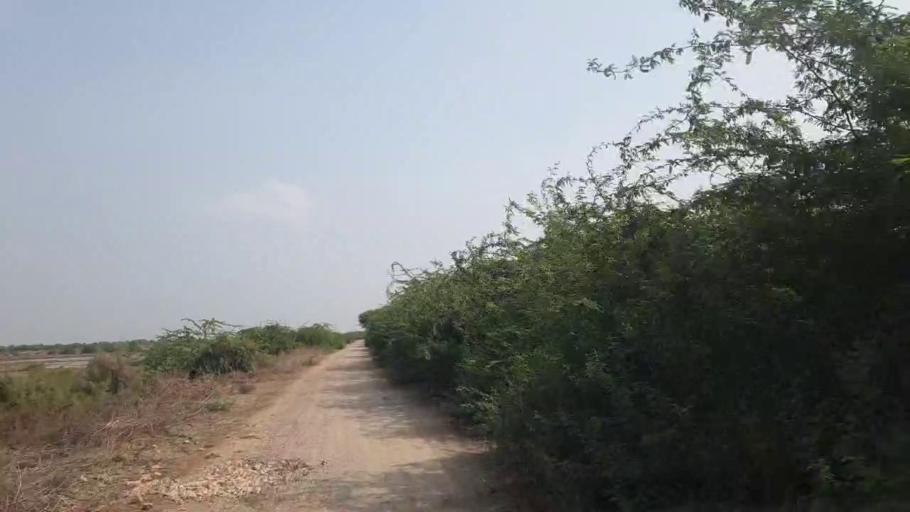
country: PK
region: Sindh
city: Badin
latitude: 24.5475
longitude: 68.6926
